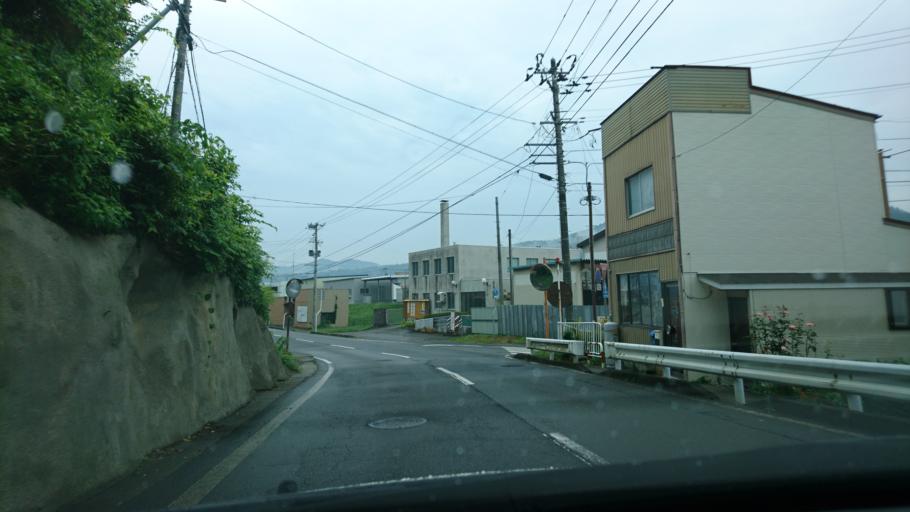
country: JP
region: Iwate
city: Ichinoseki
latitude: 38.9011
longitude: 141.2683
